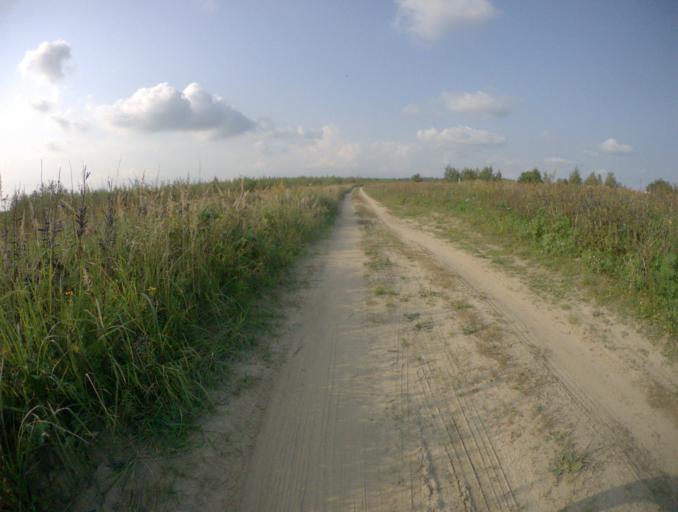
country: RU
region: Vladimir
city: Golovino
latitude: 55.9823
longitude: 40.4476
